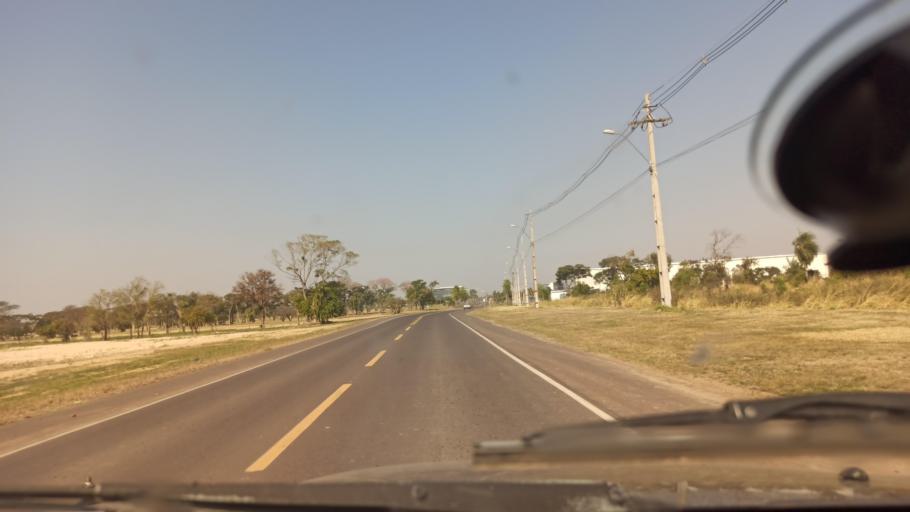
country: PY
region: Central
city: Colonia Mariano Roque Alonso
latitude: -25.1939
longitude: -57.5726
